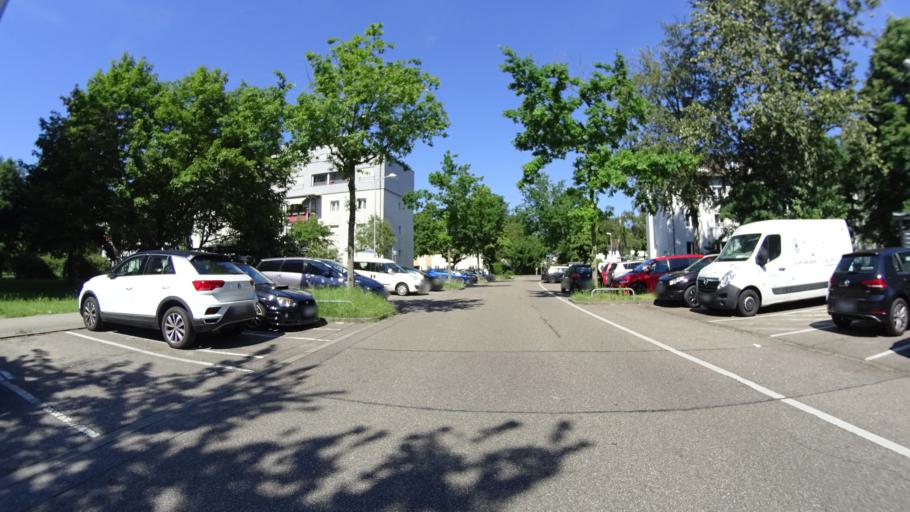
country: DE
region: Baden-Wuerttemberg
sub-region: Karlsruhe Region
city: Karlsruhe
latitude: 49.0279
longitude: 8.3917
